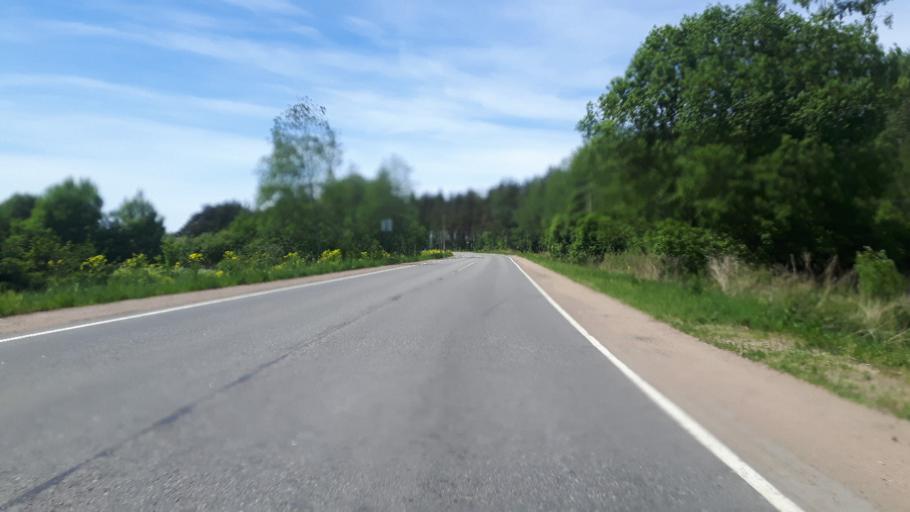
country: RU
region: Leningrad
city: Ust'-Luga
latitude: 59.5708
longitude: 28.1647
